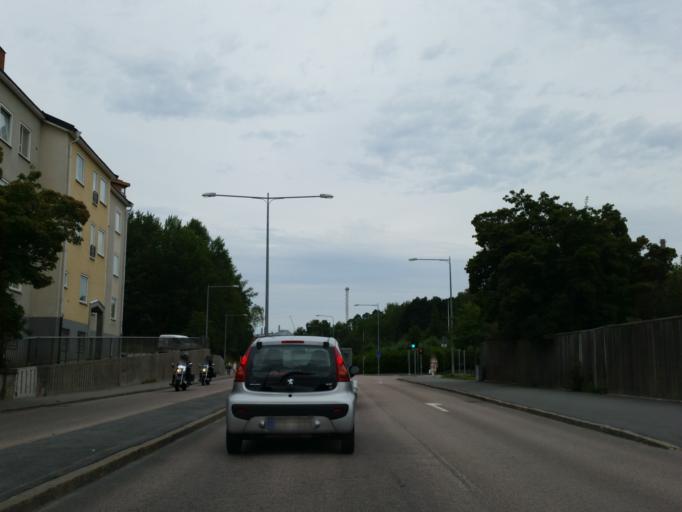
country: SE
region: Stockholm
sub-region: Sodertalje Kommun
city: Soedertaelje
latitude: 59.1995
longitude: 17.6186
